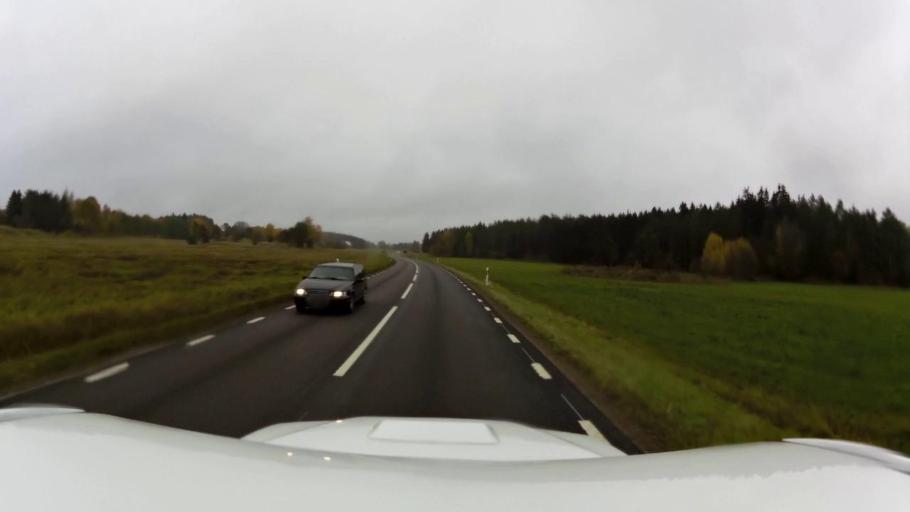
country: SE
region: OEstergoetland
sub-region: Linkopings Kommun
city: Linghem
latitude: 58.3664
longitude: 15.8208
